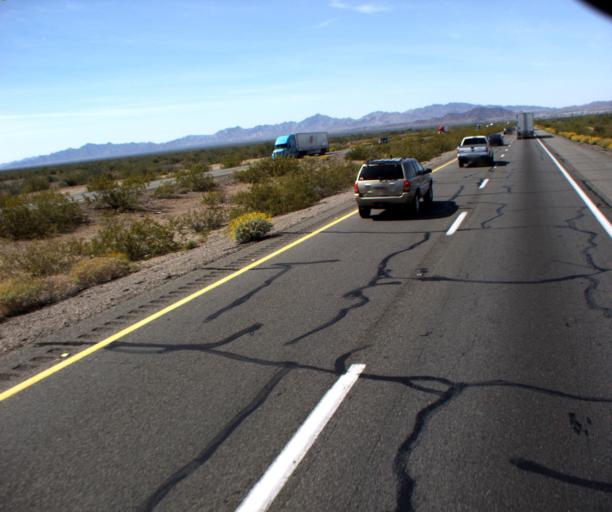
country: US
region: Arizona
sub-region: La Paz County
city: Quartzsite
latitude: 33.6747
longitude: -114.1342
